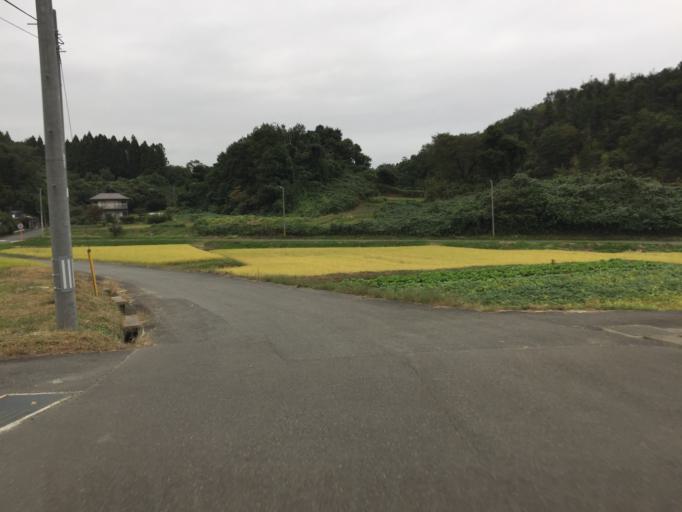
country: JP
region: Fukushima
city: Fukushima-shi
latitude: 37.6722
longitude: 140.4506
